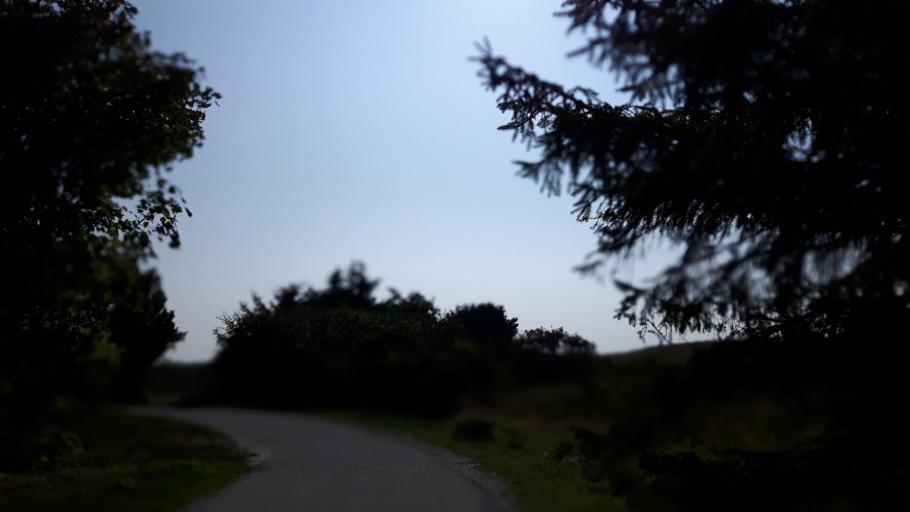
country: NL
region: Friesland
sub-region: Gemeente Ameland
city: Nes
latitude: 53.4591
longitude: 5.7888
